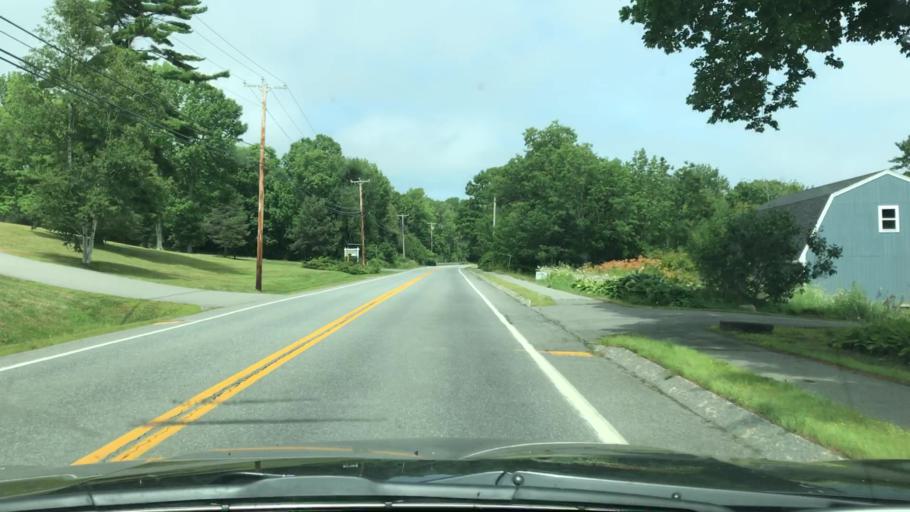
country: US
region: Maine
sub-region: Knox County
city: Camden
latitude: 44.2250
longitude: -69.0509
